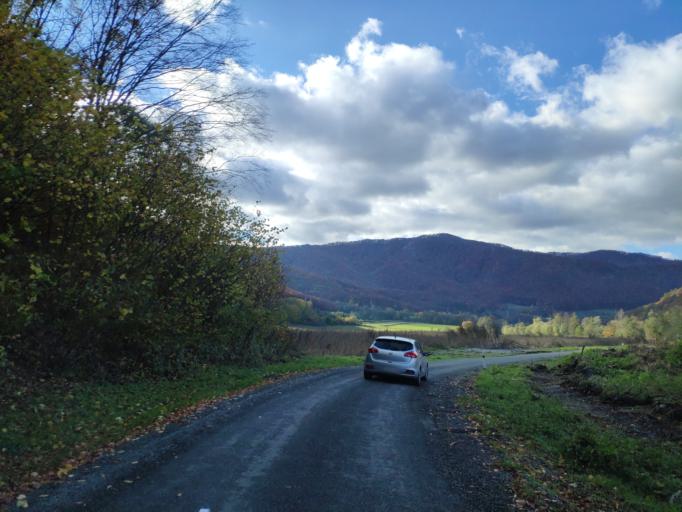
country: SK
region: Presovsky
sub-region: Okres Presov
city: Presov
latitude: 48.8530
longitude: 21.1788
